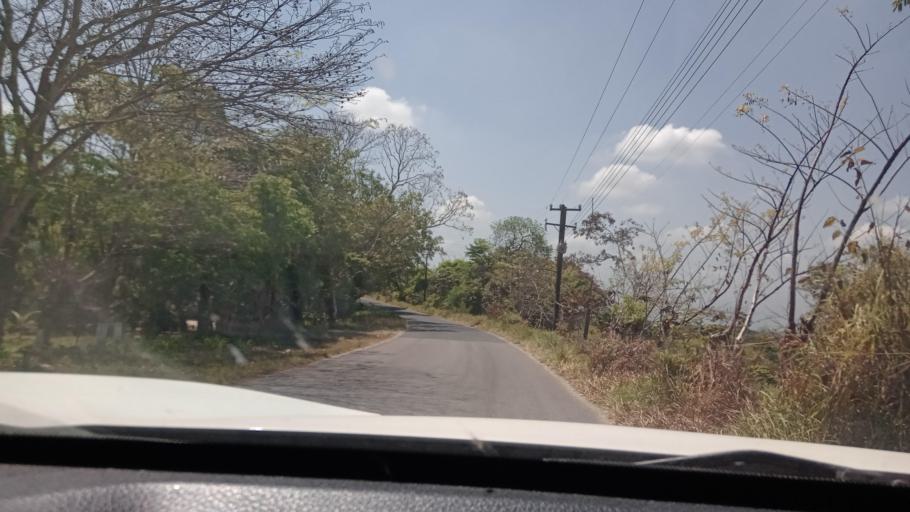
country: MX
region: Veracruz
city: Las Choapas
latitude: 17.7525
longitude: -94.1127
